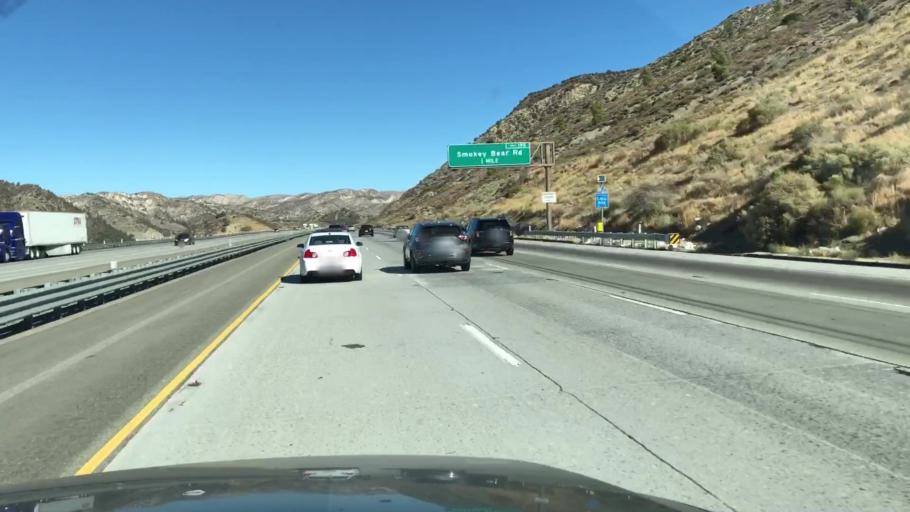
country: US
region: California
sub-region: Kern County
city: Lebec
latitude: 34.6914
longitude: -118.7886
